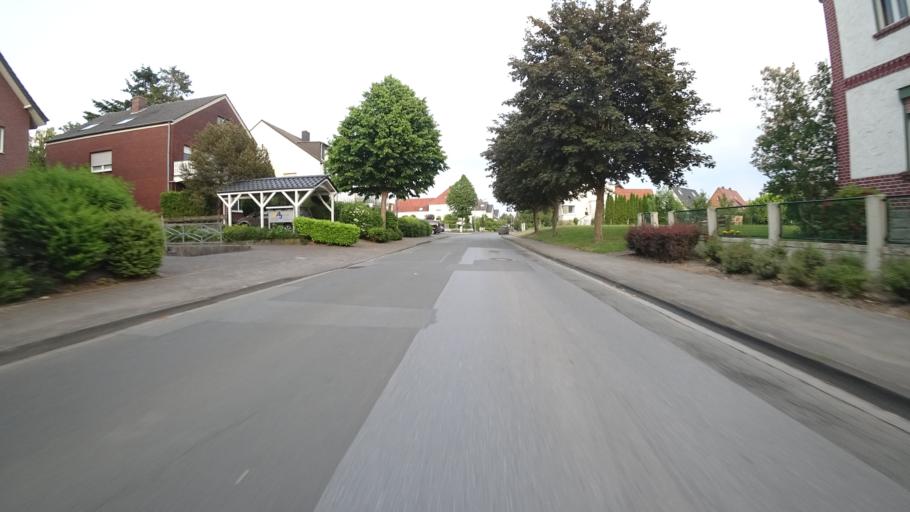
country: DE
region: North Rhine-Westphalia
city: Erwitte
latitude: 51.6360
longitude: 8.3576
